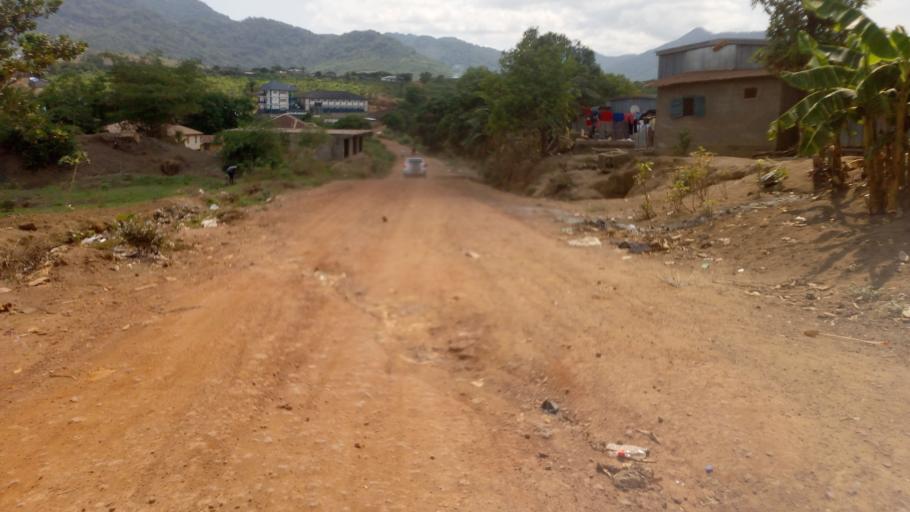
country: SL
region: Western Area
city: Waterloo
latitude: 8.3071
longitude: -13.0793
